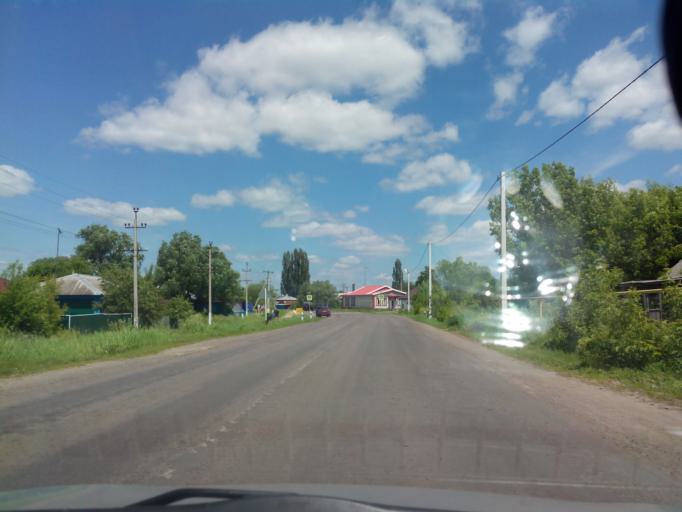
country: RU
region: Voronezj
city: Ternovka
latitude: 51.6828
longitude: 41.5788
